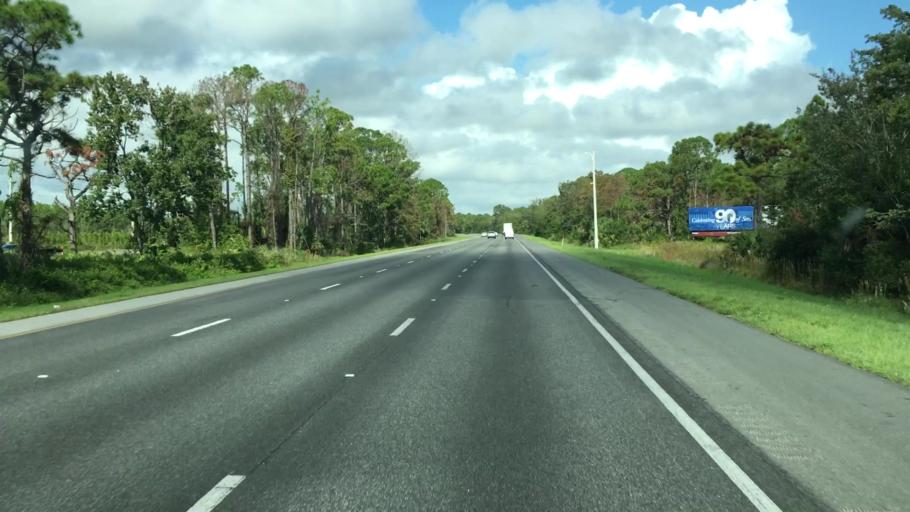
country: US
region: Florida
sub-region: Volusia County
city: Glencoe
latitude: 29.0602
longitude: -81.0079
